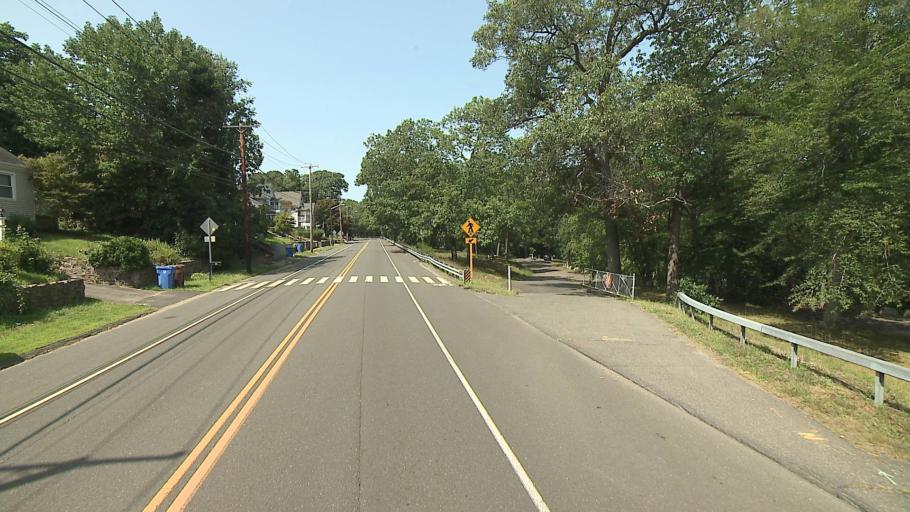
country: US
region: Connecticut
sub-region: Fairfield County
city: Shelton
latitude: 41.3229
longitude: -73.1022
